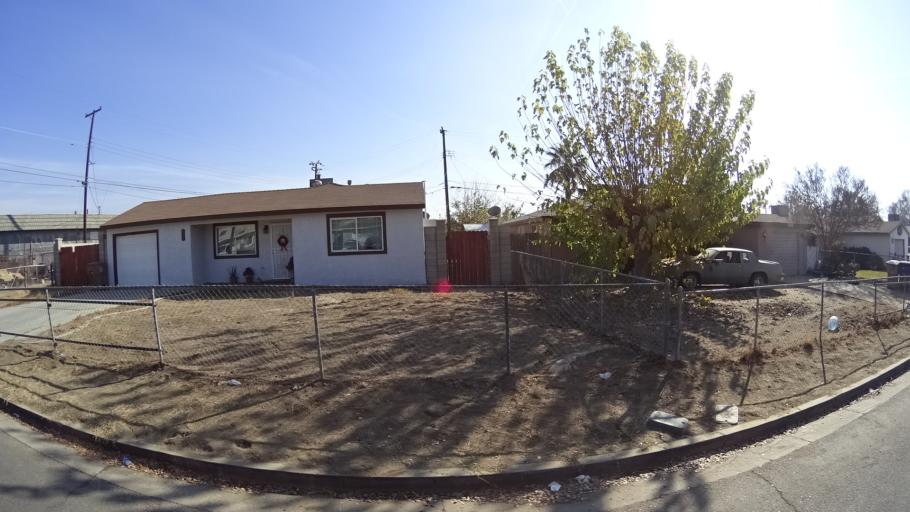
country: US
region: California
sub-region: Kern County
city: Bakersfield
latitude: 35.3287
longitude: -119.0130
